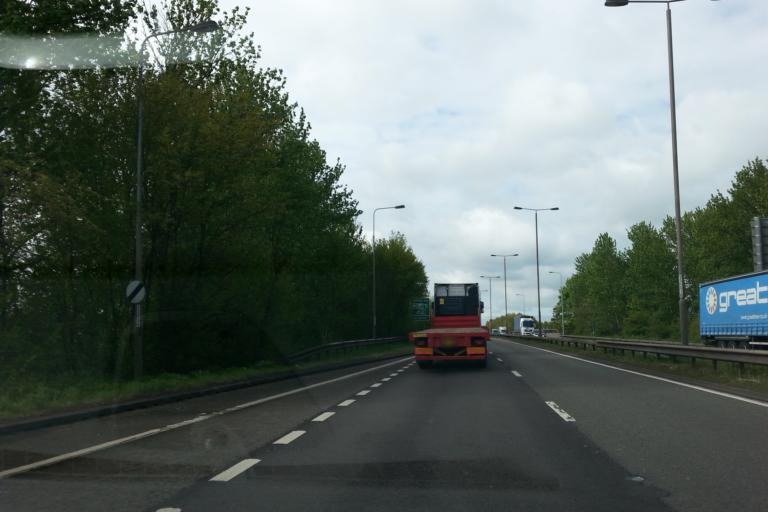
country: GB
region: England
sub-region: Derbyshire
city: Repton
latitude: 52.8608
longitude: -1.5747
